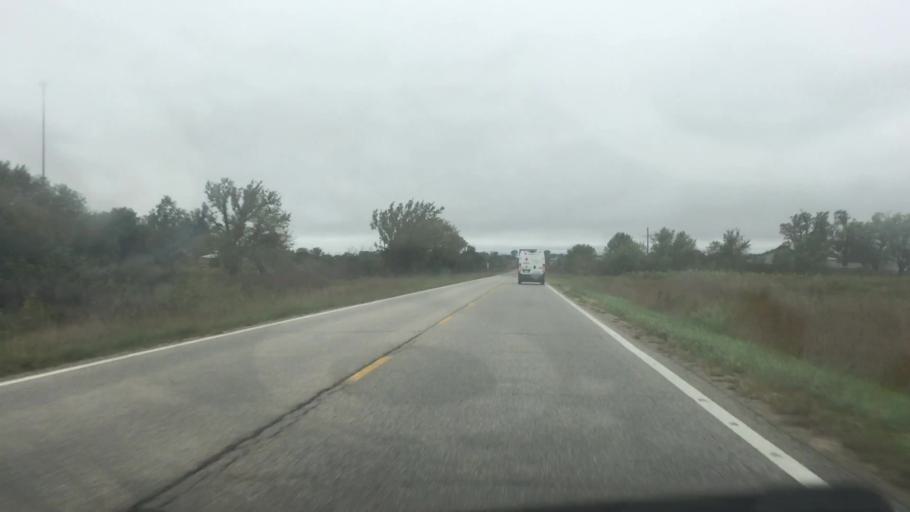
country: US
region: Kansas
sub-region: Anderson County
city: Garnett
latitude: 38.1739
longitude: -95.2778
